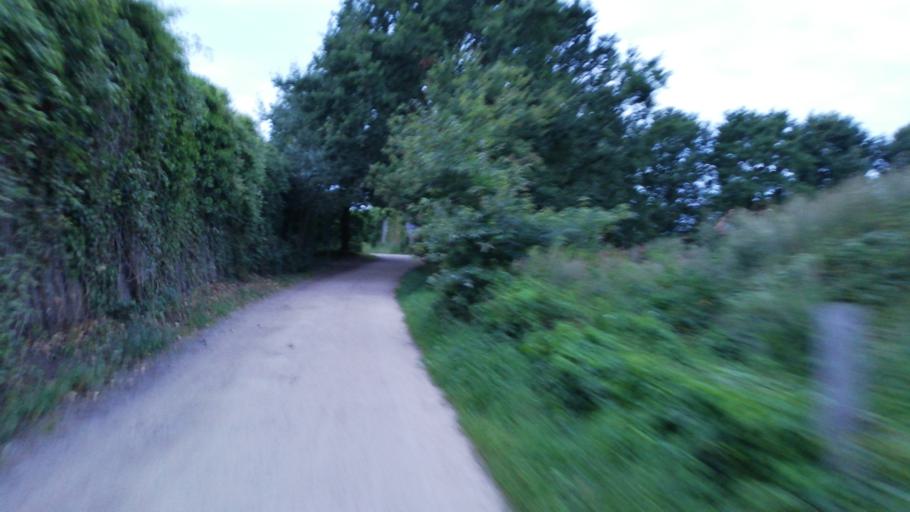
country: DE
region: Lower Saxony
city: Neu Wulmstorf
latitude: 53.4738
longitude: 9.7992
